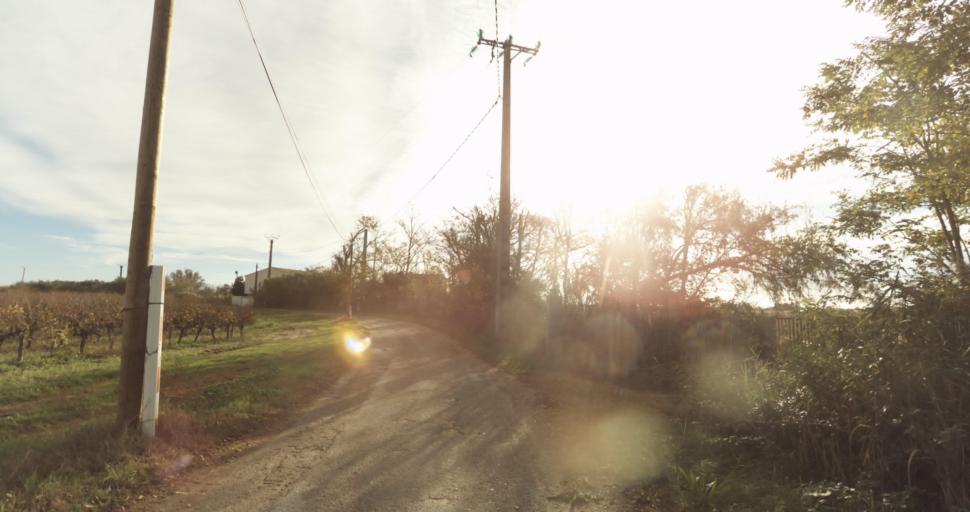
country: FR
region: Languedoc-Roussillon
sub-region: Departement du Gard
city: Aigues-Mortes
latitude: 43.5596
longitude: 4.2195
